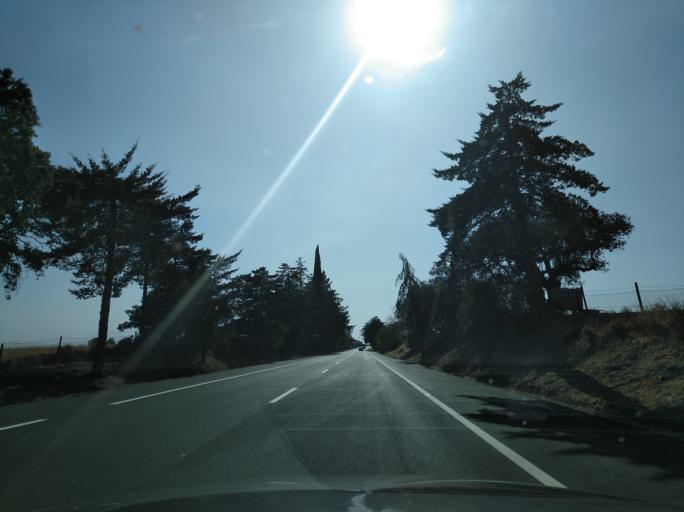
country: ES
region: Andalusia
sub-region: Provincia de Huelva
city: Rosal de la Frontera
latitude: 37.9509
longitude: -7.2951
